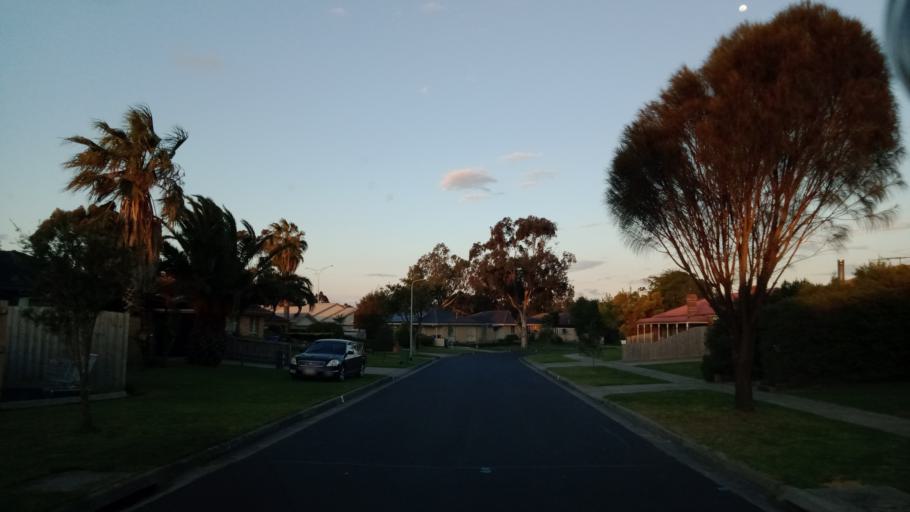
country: AU
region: Victoria
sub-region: Casey
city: Cranbourne North
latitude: -38.0822
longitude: 145.2679
